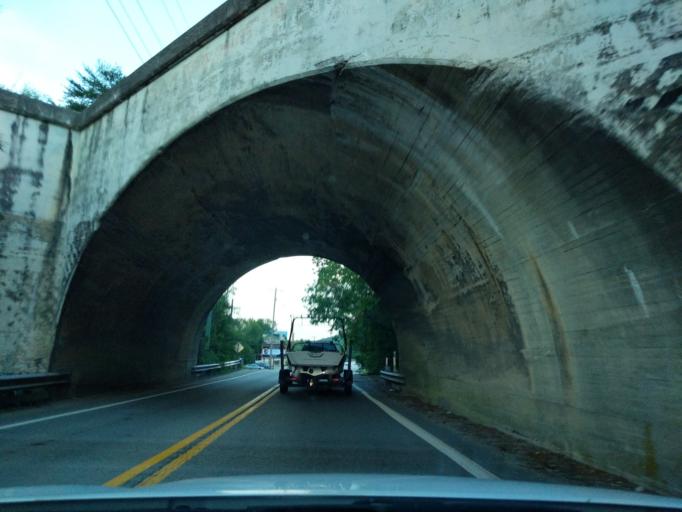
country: US
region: Tennessee
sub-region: Hamilton County
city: Lookout Mountain
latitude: 35.0207
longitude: -85.3635
